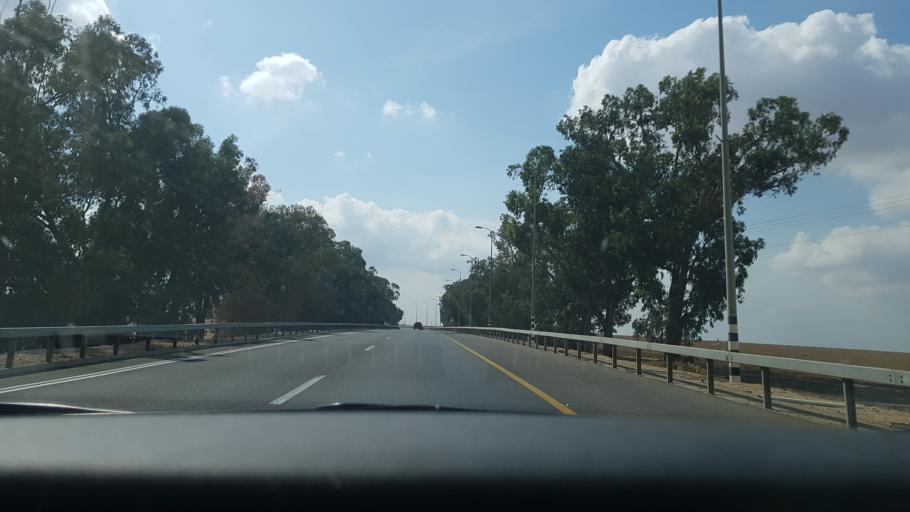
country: IL
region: Southern District
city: Lehavim
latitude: 31.4815
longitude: 34.7751
